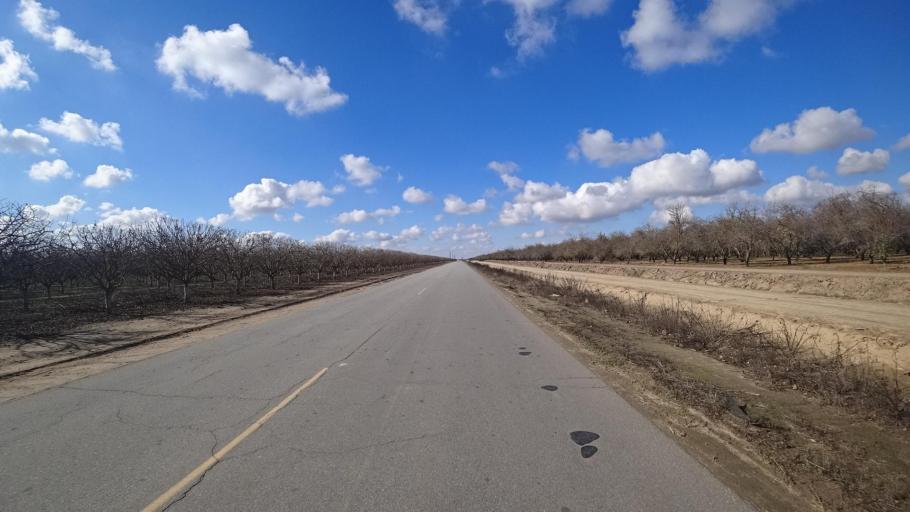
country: US
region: California
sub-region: Kern County
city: McFarland
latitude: 35.6742
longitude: -119.3127
